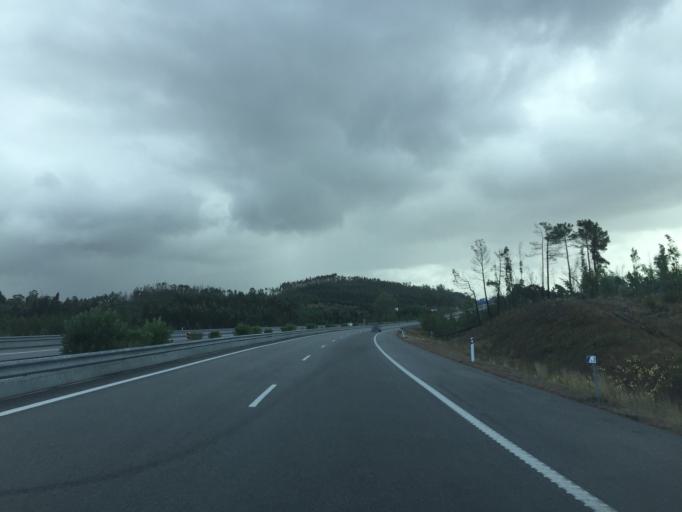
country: PT
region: Aveiro
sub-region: Mealhada
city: Pampilhosa do Botao
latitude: 40.2841
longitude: -8.5144
